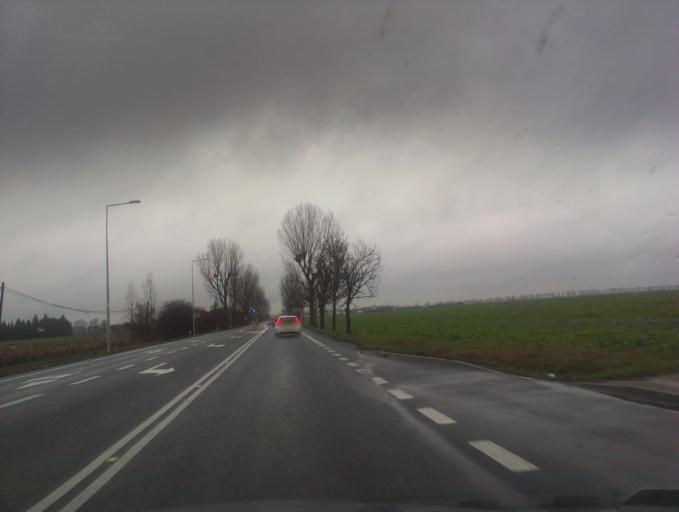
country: PL
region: Greater Poland Voivodeship
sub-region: Powiat obornicki
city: Oborniki
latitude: 52.5815
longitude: 16.8281
